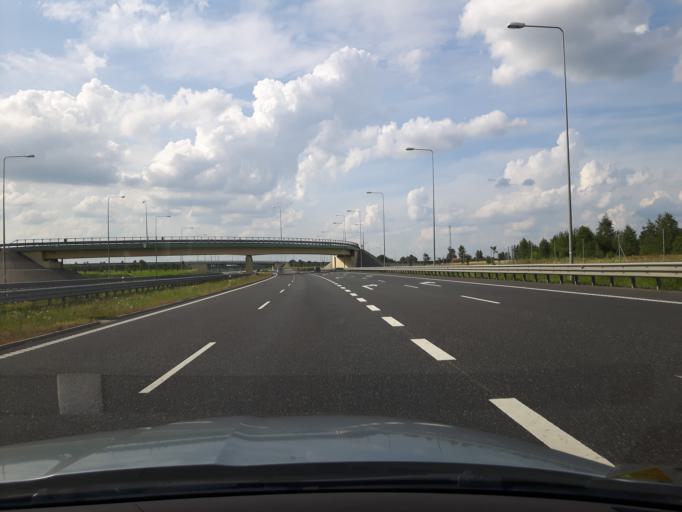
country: PL
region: Warmian-Masurian Voivodeship
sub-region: Powiat olsztynski
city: Olsztynek
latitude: 53.5800
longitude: 20.2559
